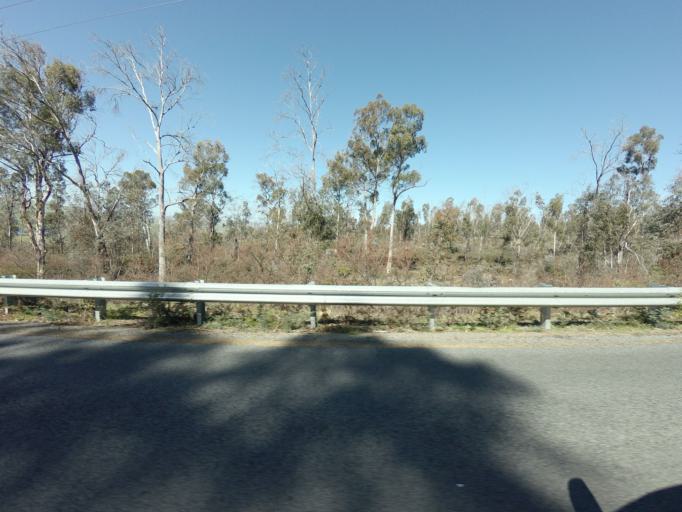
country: AU
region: Tasmania
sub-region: Derwent Valley
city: New Norfolk
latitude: -42.5426
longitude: 146.7188
